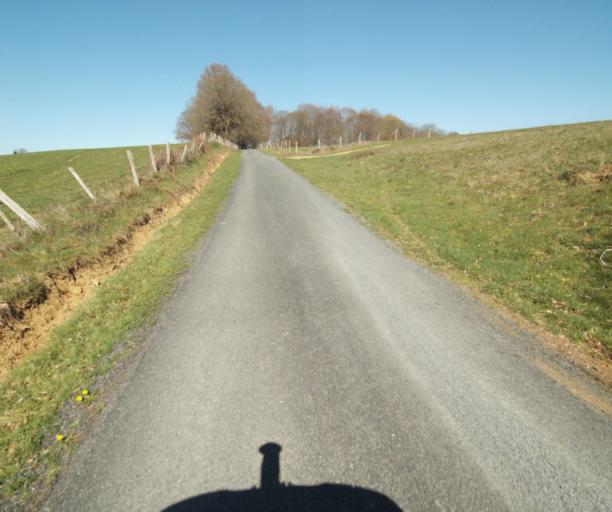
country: FR
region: Limousin
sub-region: Departement de la Correze
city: Saint-Clement
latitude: 45.3490
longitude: 1.6681
